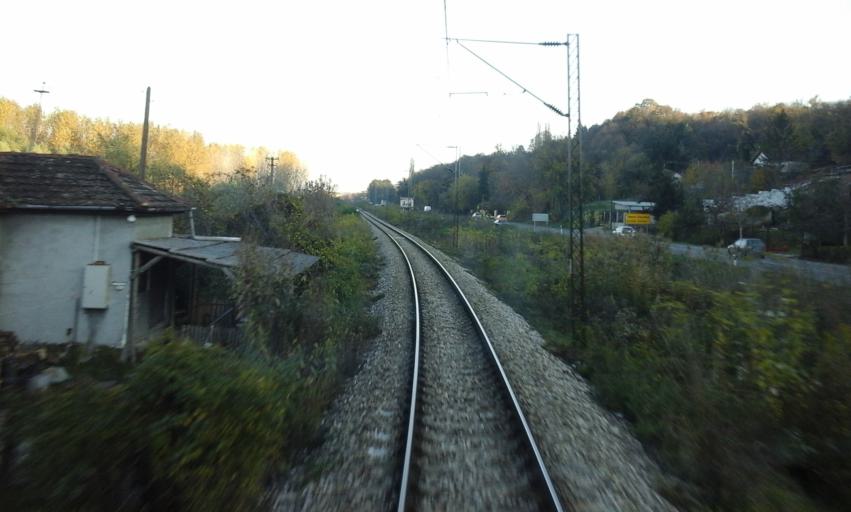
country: RS
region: Autonomna Pokrajina Vojvodina
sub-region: Juznobacki Okrug
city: Sremski Karlovci
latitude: 45.2142
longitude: 19.9124
